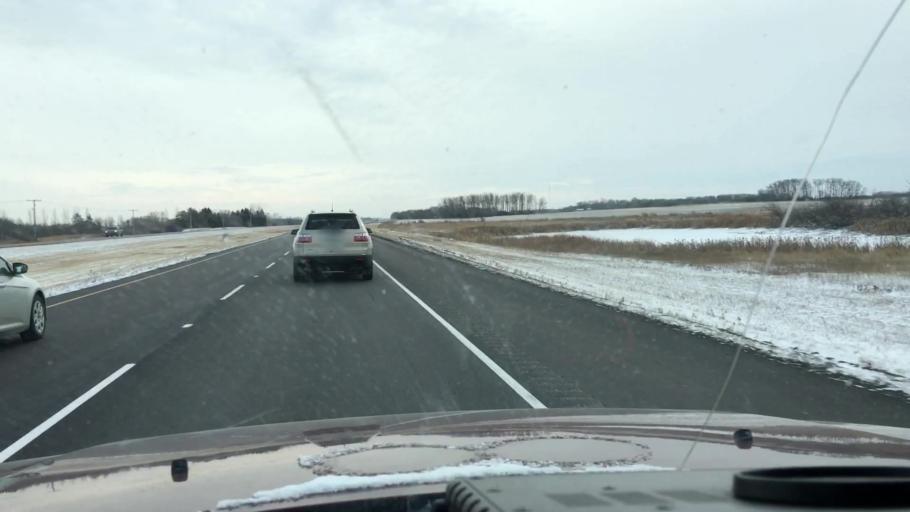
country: CA
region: Saskatchewan
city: Saskatoon
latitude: 52.0194
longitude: -106.5775
